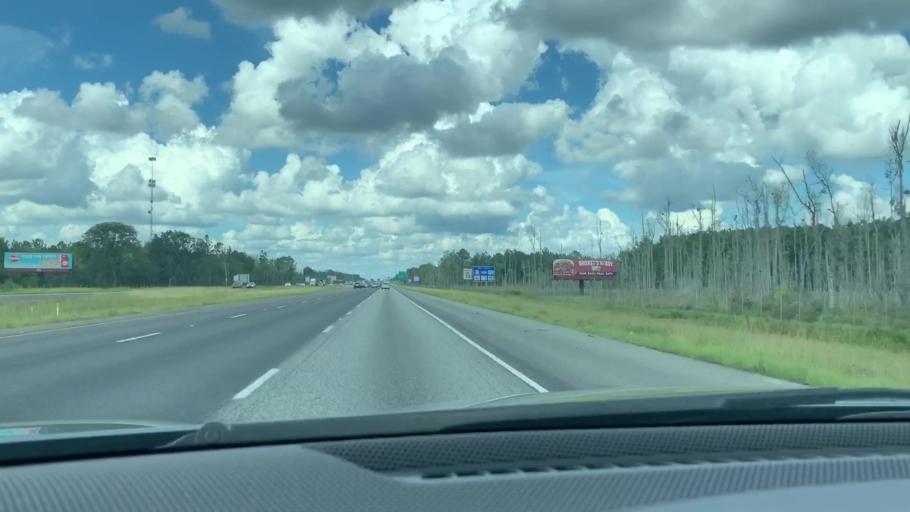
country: US
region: Georgia
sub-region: Camden County
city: Kingsland
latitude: 30.7706
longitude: -81.6545
